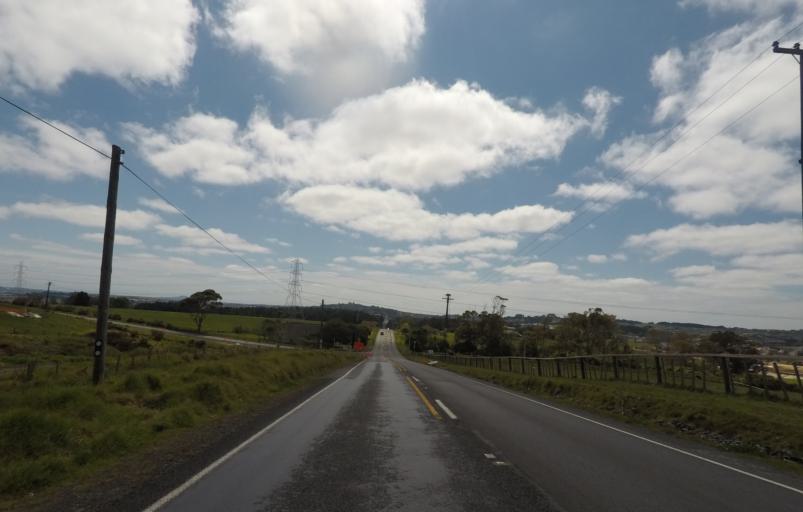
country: NZ
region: Auckland
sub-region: Auckland
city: Manukau City
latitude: -36.9874
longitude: 174.9190
